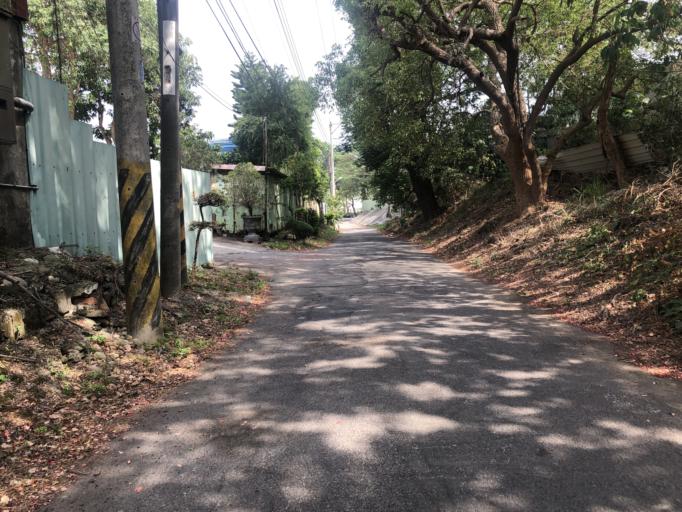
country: TW
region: Taiwan
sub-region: Changhua
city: Chang-hua
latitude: 24.1365
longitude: 120.6024
